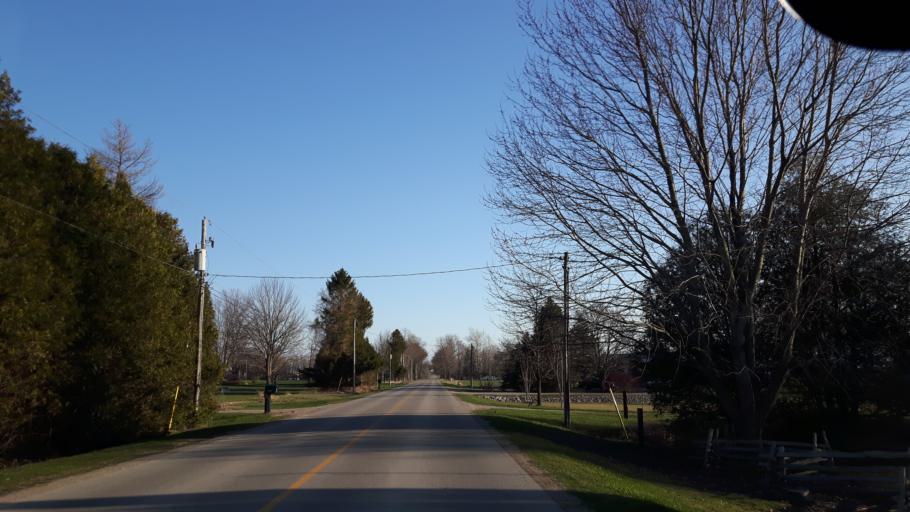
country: CA
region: Ontario
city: Goderich
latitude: 43.7100
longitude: -81.6851
